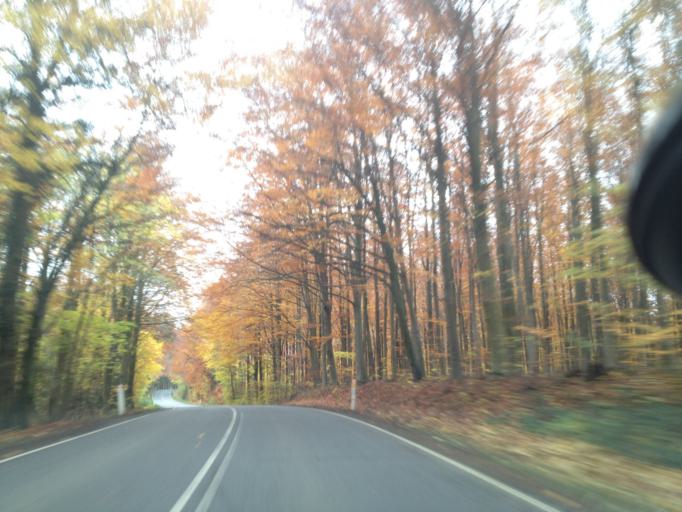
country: DK
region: South Denmark
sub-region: Assens Kommune
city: Vissenbjerg
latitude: 55.4456
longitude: 10.1672
